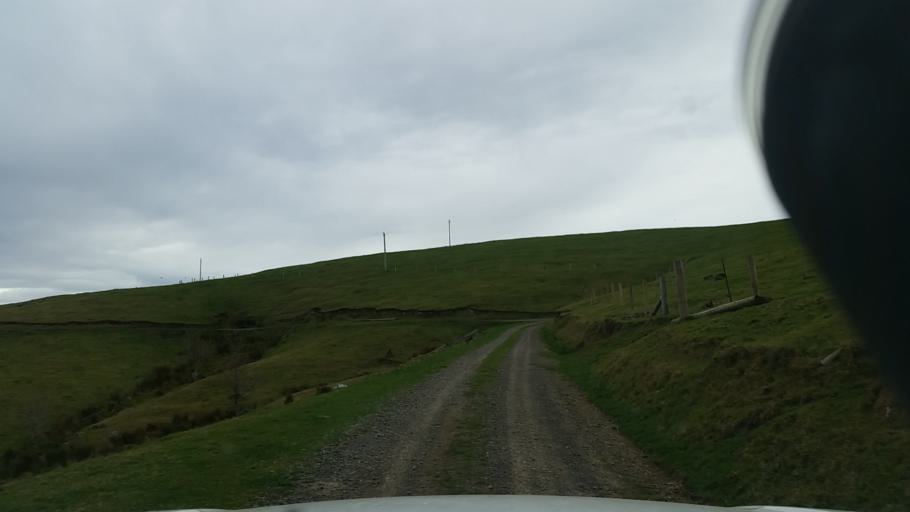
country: NZ
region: Canterbury
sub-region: Christchurch City
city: Christchurch
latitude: -43.8613
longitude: 173.0287
